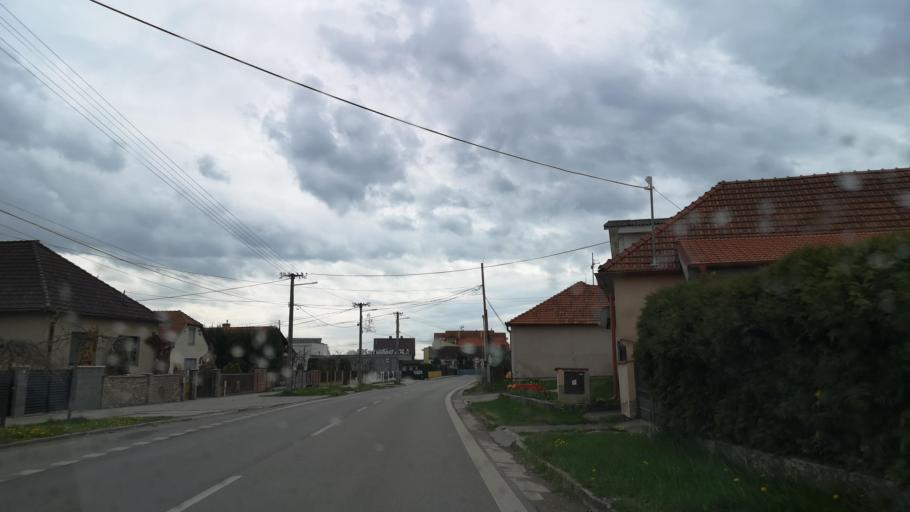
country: SK
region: Nitriansky
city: Zlate Moravce
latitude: 48.3383
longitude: 18.3569
